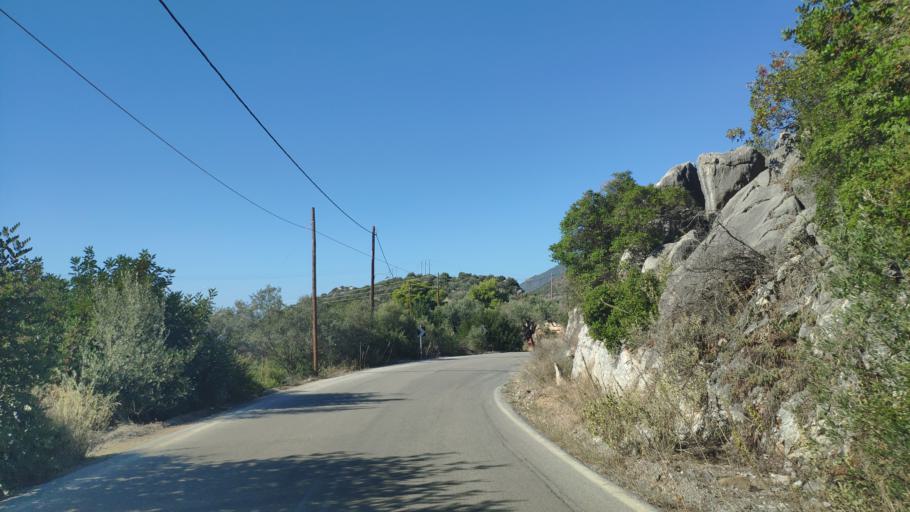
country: GR
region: Attica
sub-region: Nomos Piraios
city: Galatas
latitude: 37.5504
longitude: 23.3725
